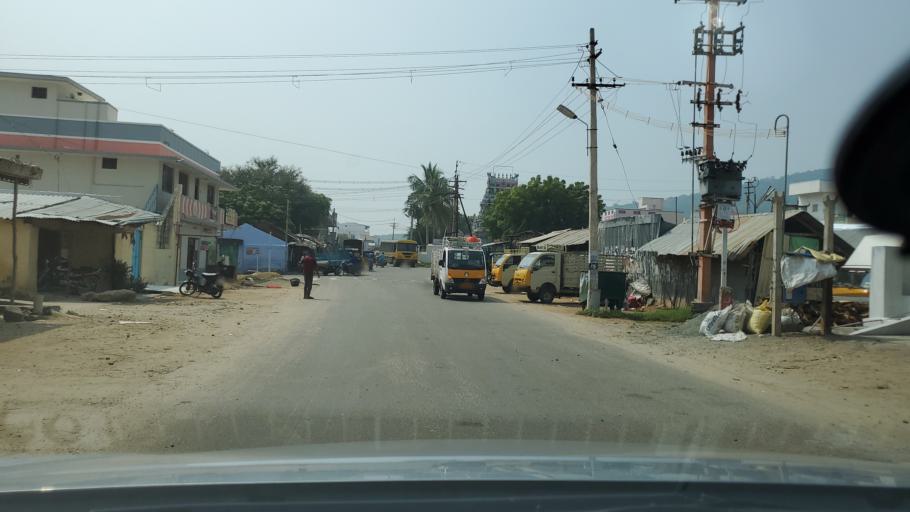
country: IN
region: Tamil Nadu
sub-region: Erode
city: Chennimalai
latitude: 11.1669
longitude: 77.6023
